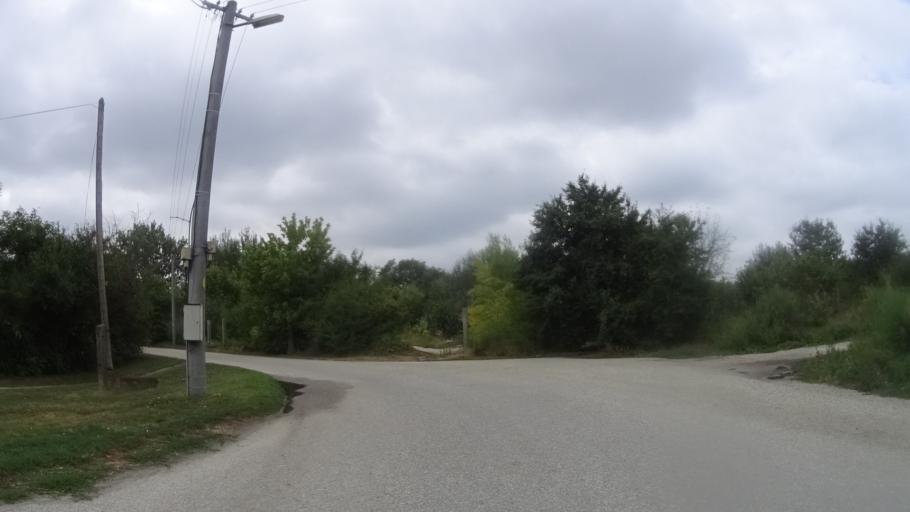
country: HU
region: Komarom-Esztergom
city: Acs
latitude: 47.7585
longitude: 17.9461
